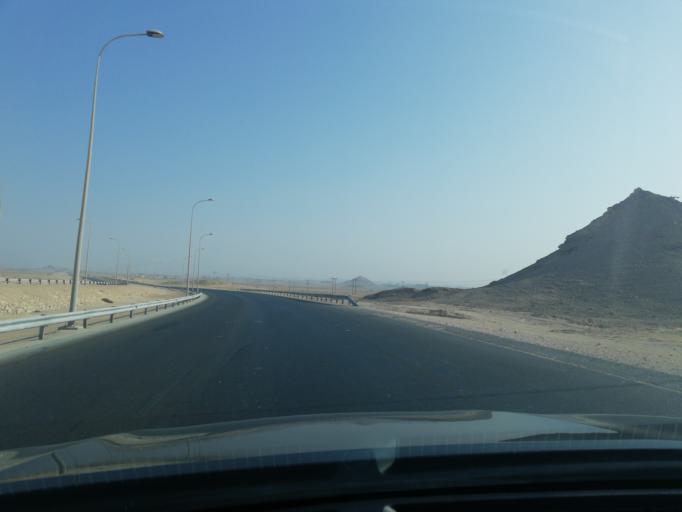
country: OM
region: Zufar
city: Salalah
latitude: 17.4167
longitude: 54.0510
